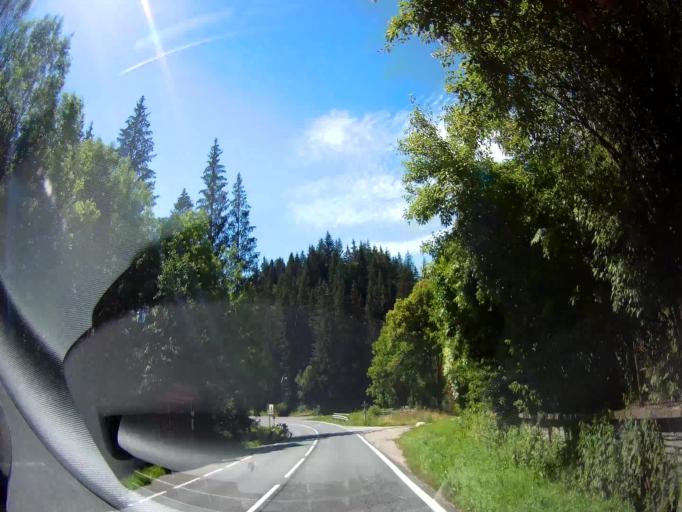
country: AT
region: Carinthia
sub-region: Politischer Bezirk Sankt Veit an der Glan
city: Glodnitz
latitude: 46.8528
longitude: 14.1390
